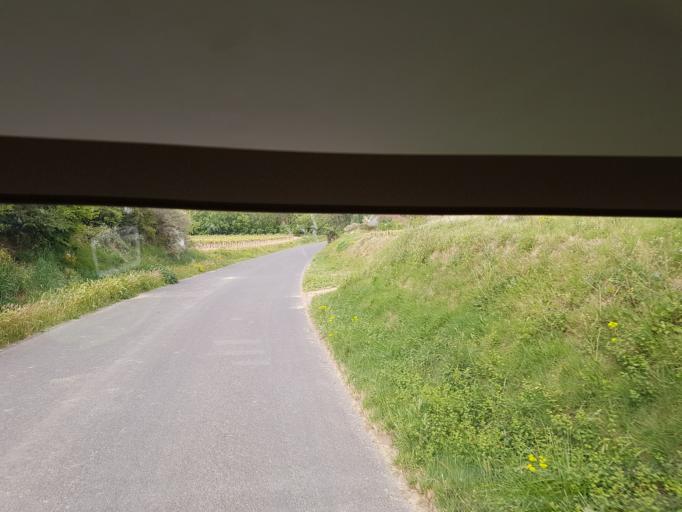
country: FR
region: Languedoc-Roussillon
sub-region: Departement de l'Aude
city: Fleury
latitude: 43.2394
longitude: 3.1466
